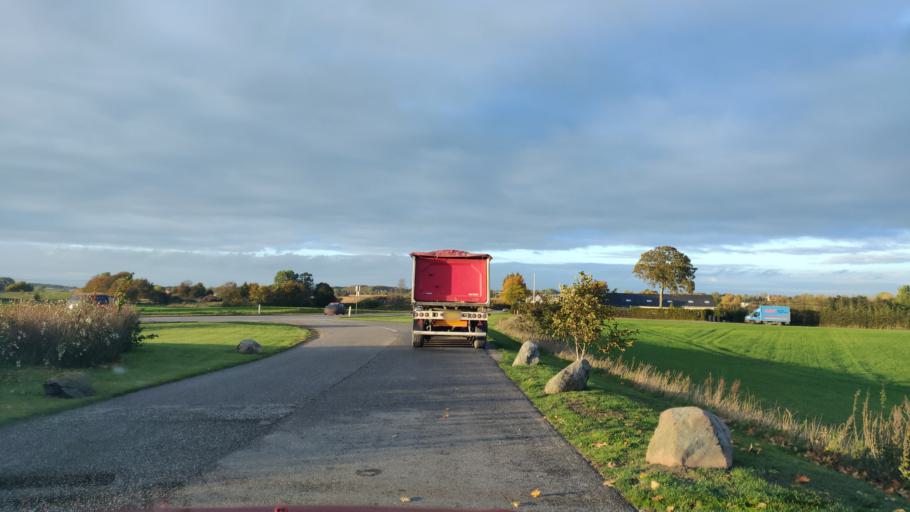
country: DK
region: Zealand
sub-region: Holbaek Kommune
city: Holbaek
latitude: 55.6777
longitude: 11.6917
